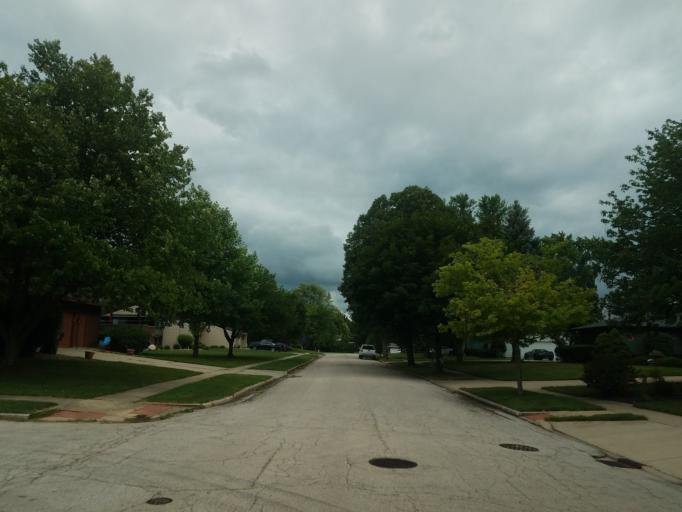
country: US
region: Illinois
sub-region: McLean County
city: Bloomington
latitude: 40.4781
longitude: -88.9462
